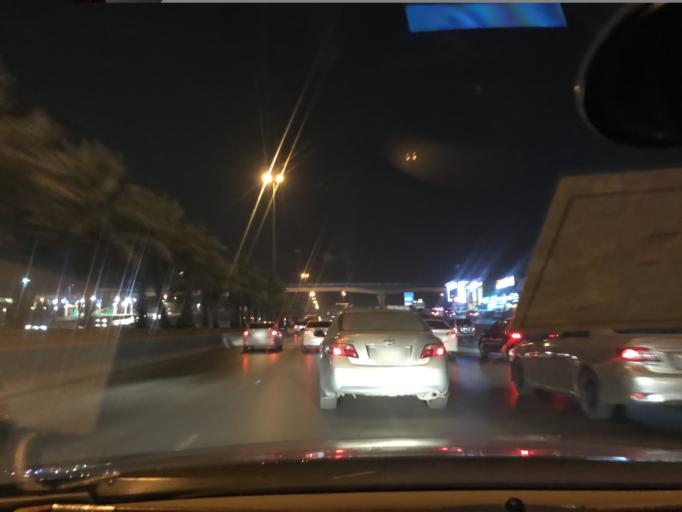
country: SA
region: Ar Riyad
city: Riyadh
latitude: 24.7575
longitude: 46.7401
